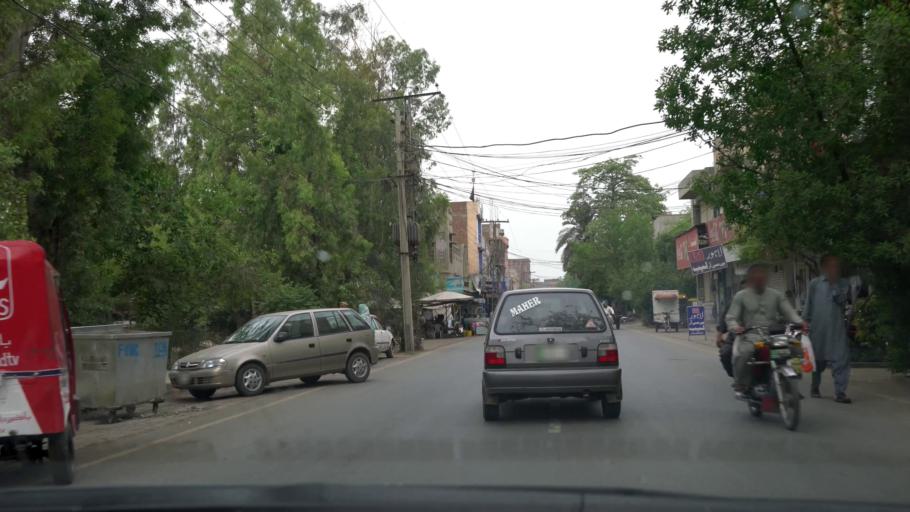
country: PK
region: Punjab
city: Faisalabad
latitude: 31.4216
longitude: 73.0675
